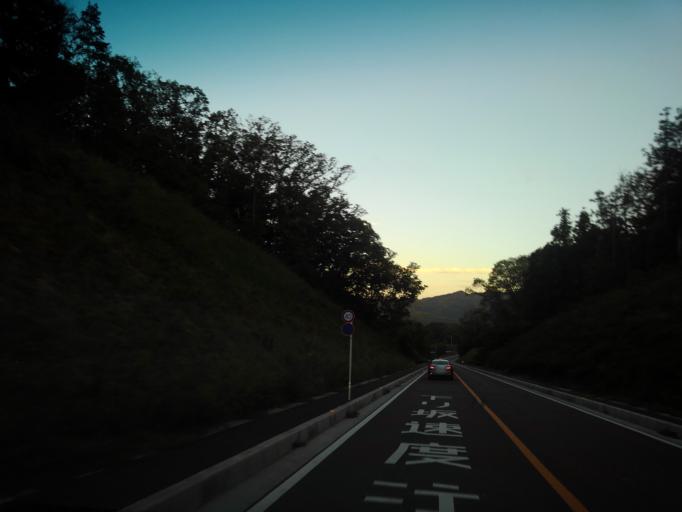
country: JP
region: Saitama
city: Hanno
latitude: 35.8752
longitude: 139.3105
